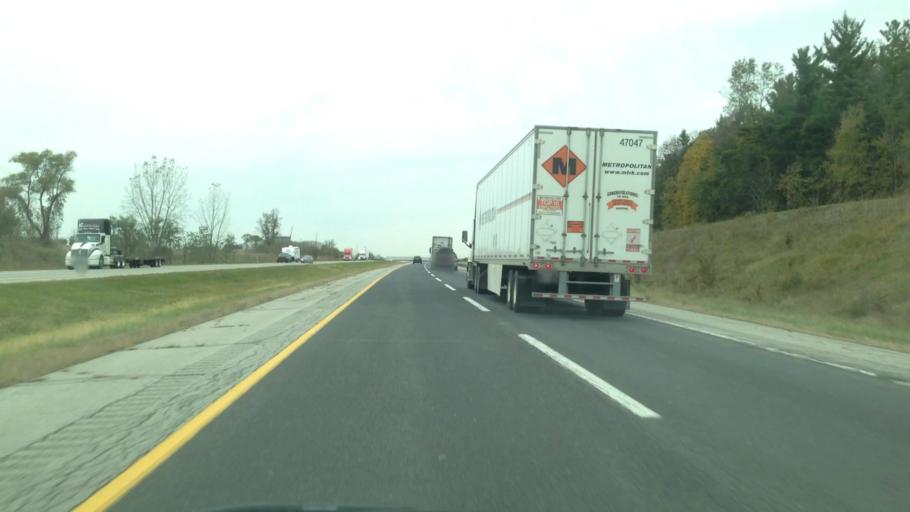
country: US
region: Indiana
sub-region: Steuben County
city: Fremont
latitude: 41.6754
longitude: -84.8704
